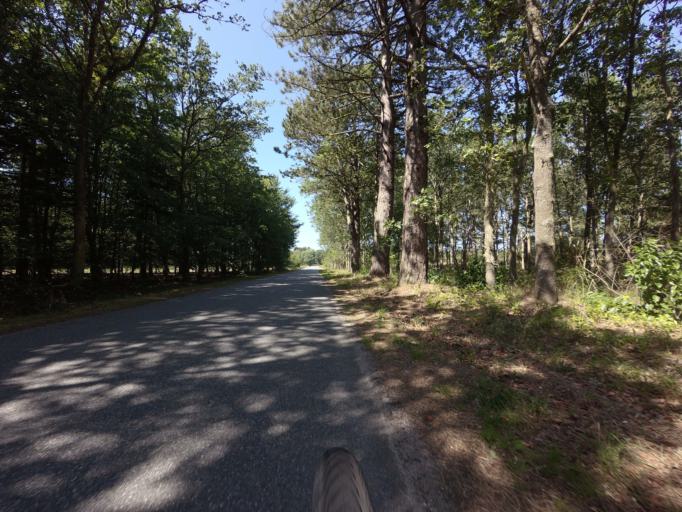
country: DK
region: North Denmark
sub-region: Laeso Kommune
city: Byrum
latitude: 57.2782
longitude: 11.0102
